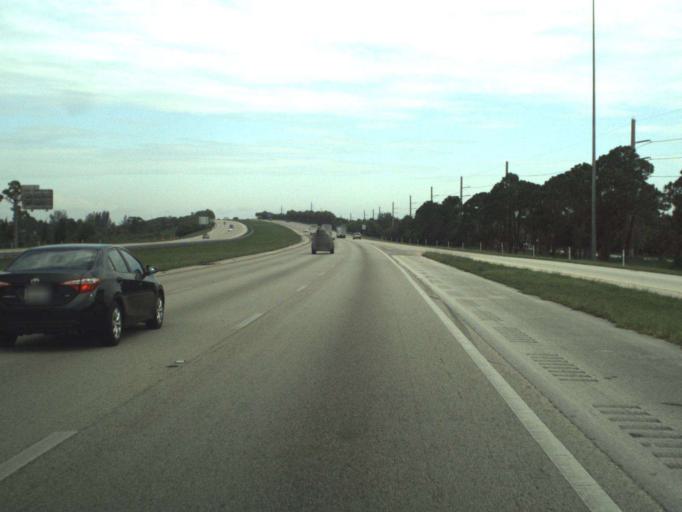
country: US
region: Florida
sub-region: Martin County
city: Palm City
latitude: 27.1128
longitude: -80.2627
